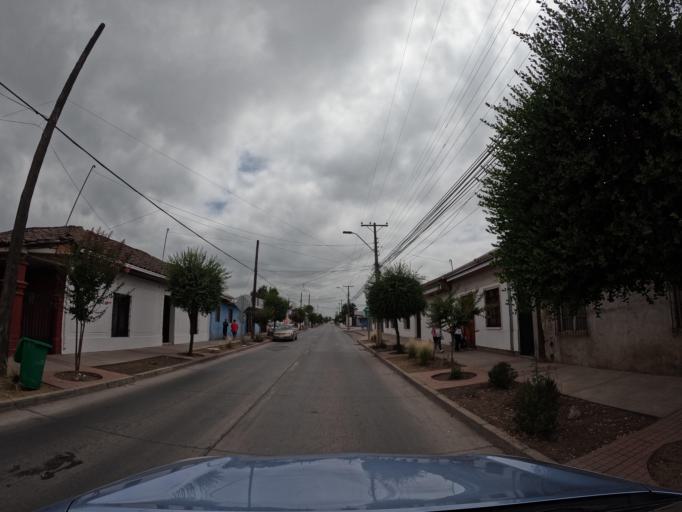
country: CL
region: O'Higgins
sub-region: Provincia de Colchagua
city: Chimbarongo
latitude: -34.7119
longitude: -71.0458
